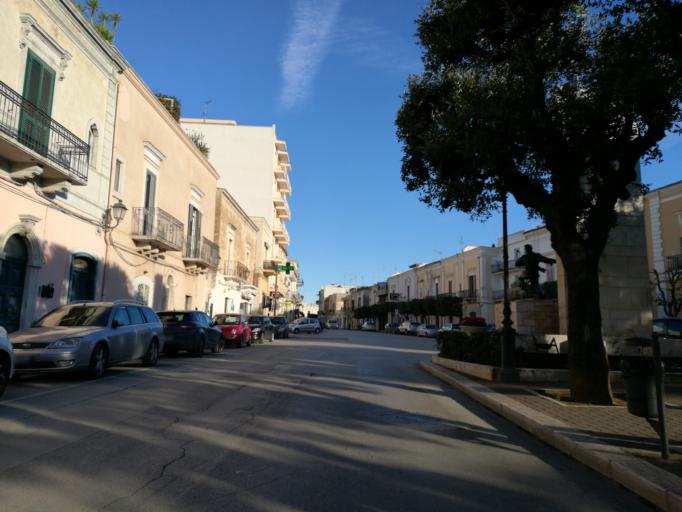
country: IT
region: Apulia
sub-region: Provincia di Bari
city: Adelfia
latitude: 41.0042
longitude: 16.8653
